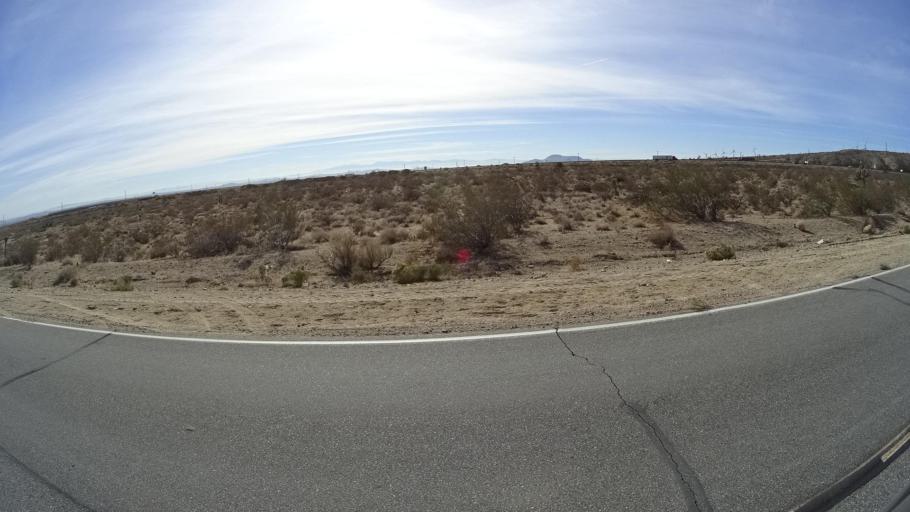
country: US
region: California
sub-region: Kern County
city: Mojave
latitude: 35.1196
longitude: -118.1935
